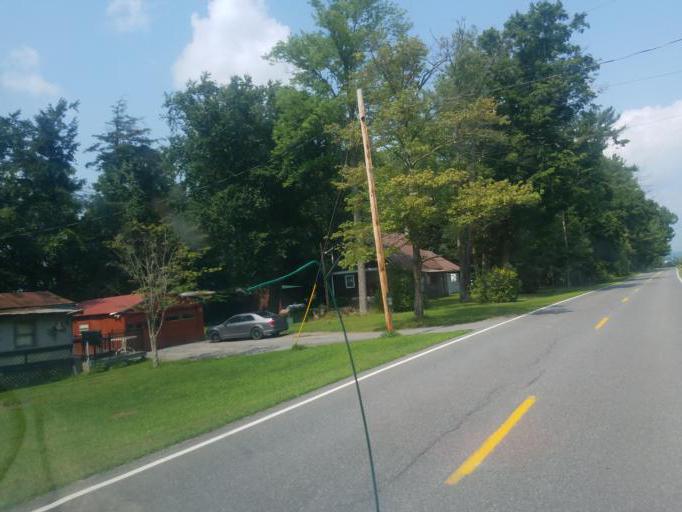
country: US
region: New York
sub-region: Montgomery County
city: Tribes Hill
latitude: 42.9206
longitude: -74.3226
